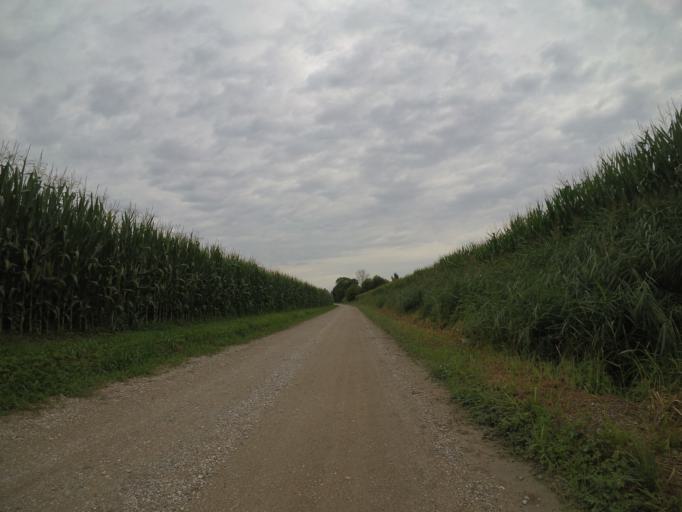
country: IT
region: Friuli Venezia Giulia
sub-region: Provincia di Udine
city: Varmo
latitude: 45.8750
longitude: 13.0115
